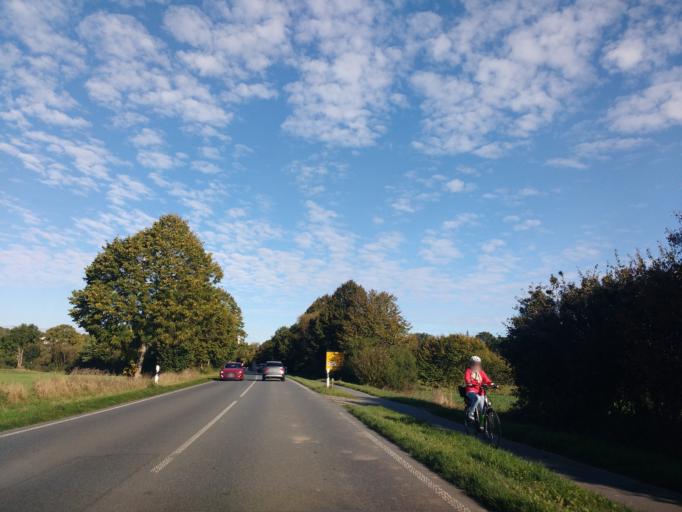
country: DE
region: Schleswig-Holstein
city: Timmendorfer Strand
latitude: 53.9852
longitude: 10.7732
